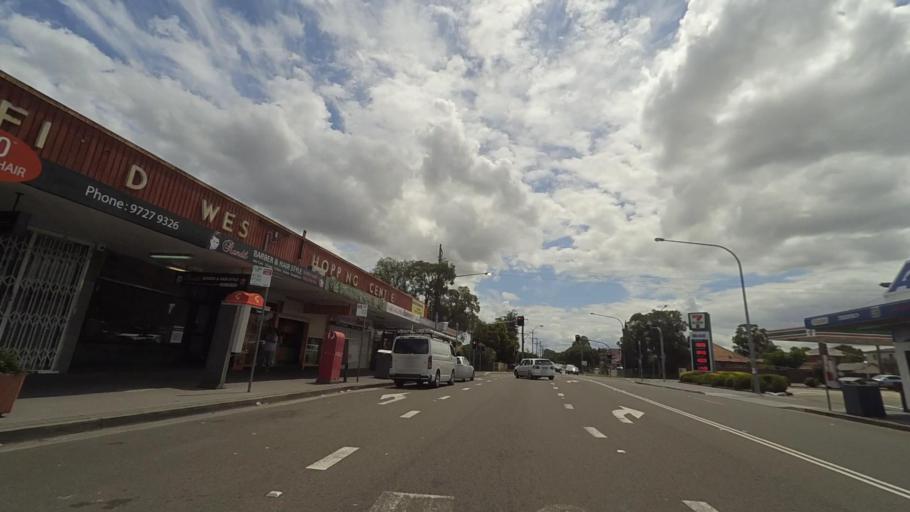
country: AU
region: New South Wales
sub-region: Fairfield
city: Fairfield Heights
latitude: -33.8725
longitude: 150.9376
